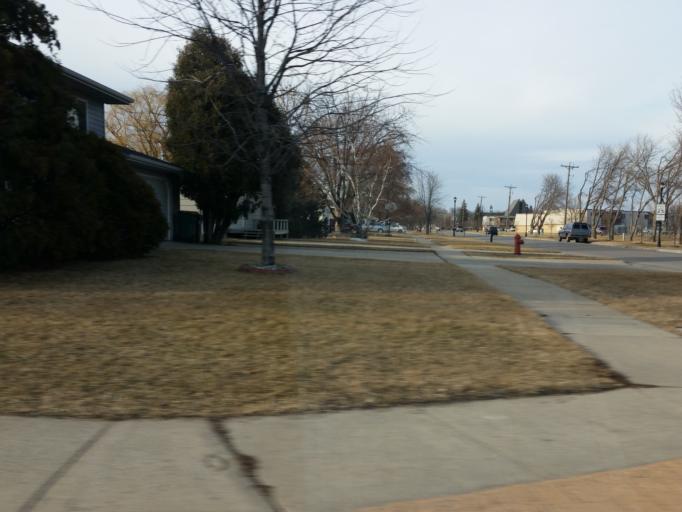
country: US
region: North Dakota
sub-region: Cass County
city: West Fargo
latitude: 46.8625
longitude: -96.9002
